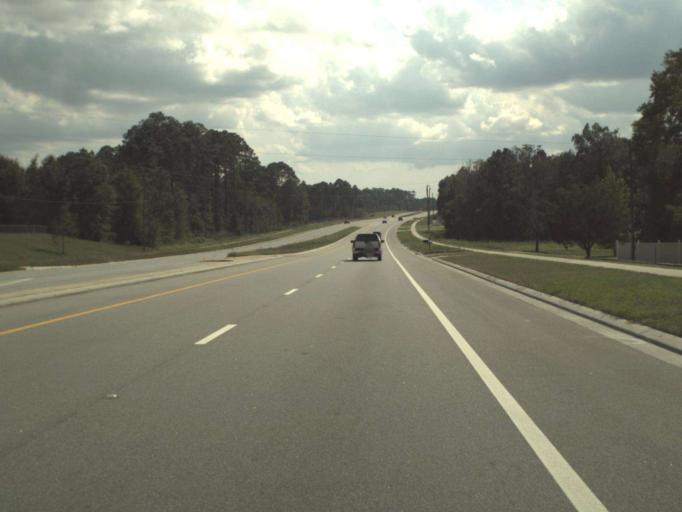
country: US
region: Florida
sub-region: Bay County
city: Laguna Beach
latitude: 30.4398
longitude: -85.8742
